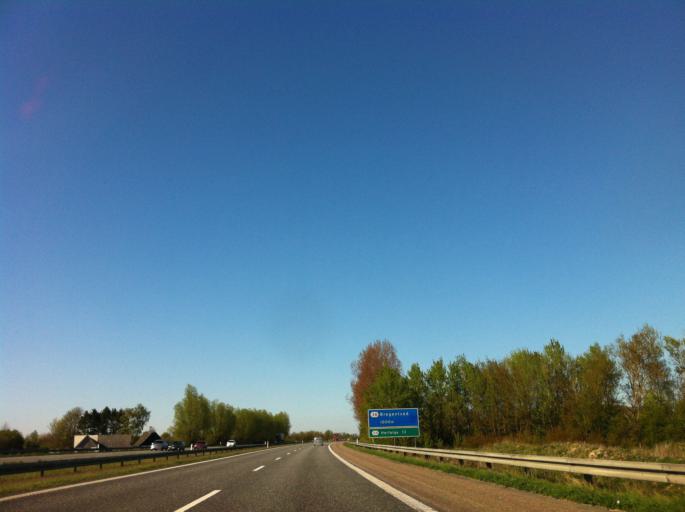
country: DK
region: Zealand
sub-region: Faxe Kommune
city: Ronnede
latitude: 55.2754
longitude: 12.0088
